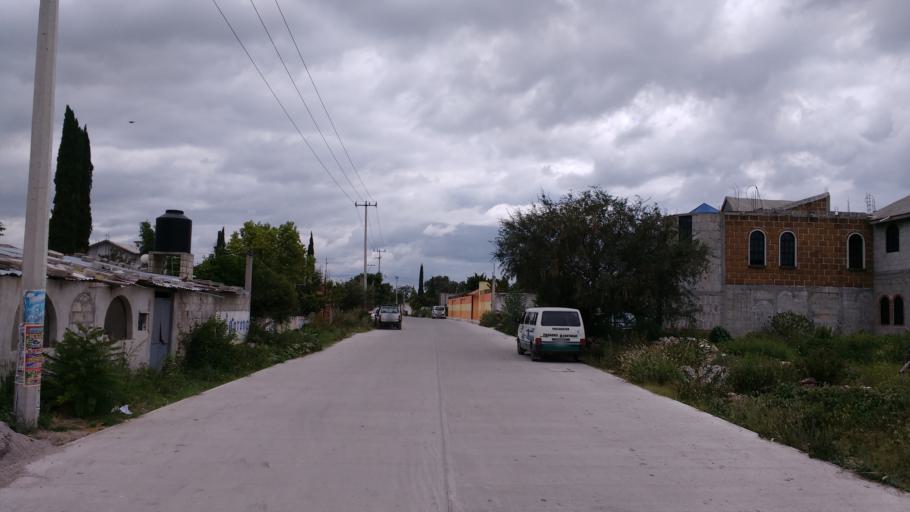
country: MX
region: Hidalgo
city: Mixquiahuala de Juarez
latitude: 20.2328
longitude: -99.2484
